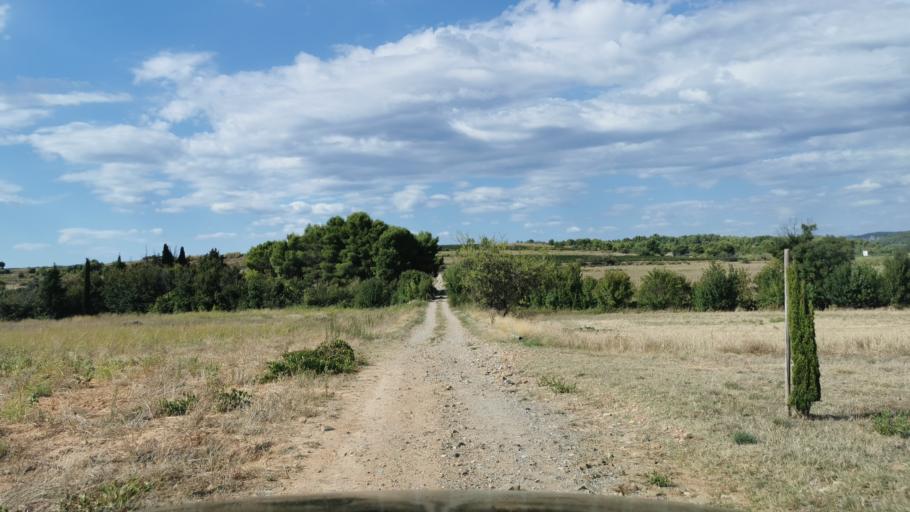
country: FR
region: Languedoc-Roussillon
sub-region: Departement de l'Aude
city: Ginestas
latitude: 43.2857
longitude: 2.8632
